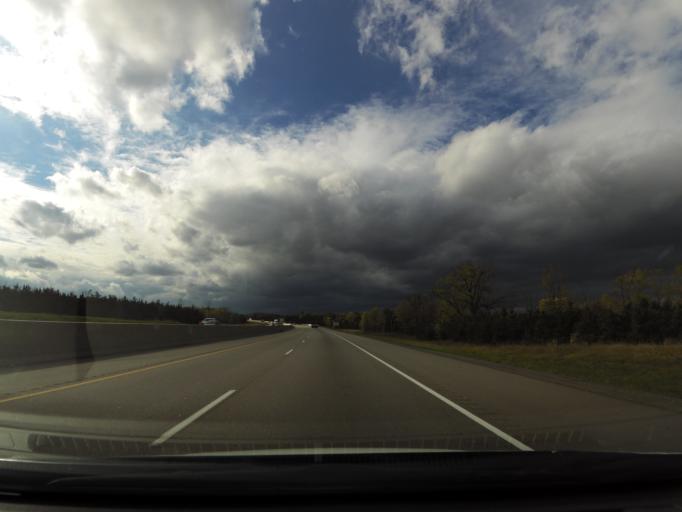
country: CA
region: Ontario
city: Belleville
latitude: 44.2214
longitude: -77.2804
